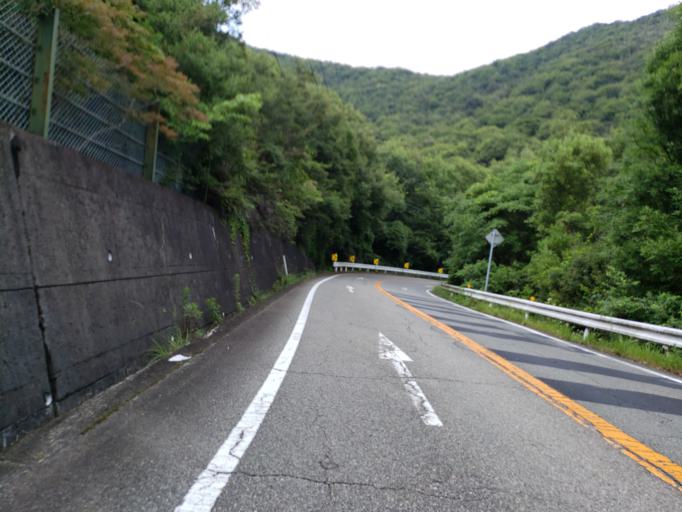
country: JP
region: Hyogo
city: Aioi
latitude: 34.7678
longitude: 134.4798
